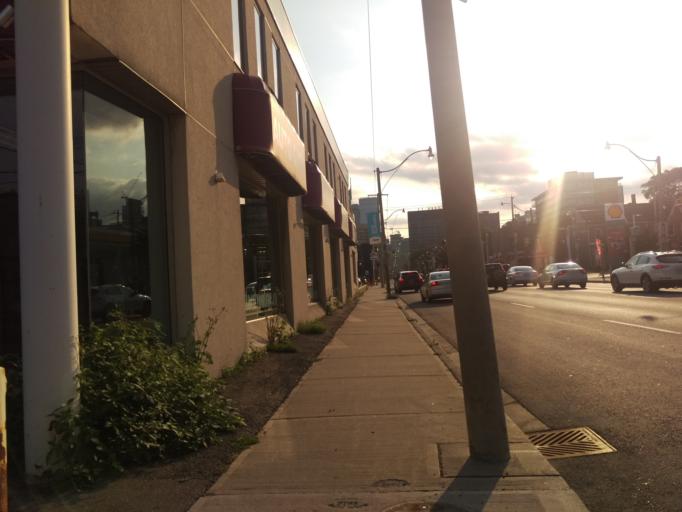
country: CA
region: Ontario
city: Toronto
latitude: 43.6547
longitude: -79.3631
